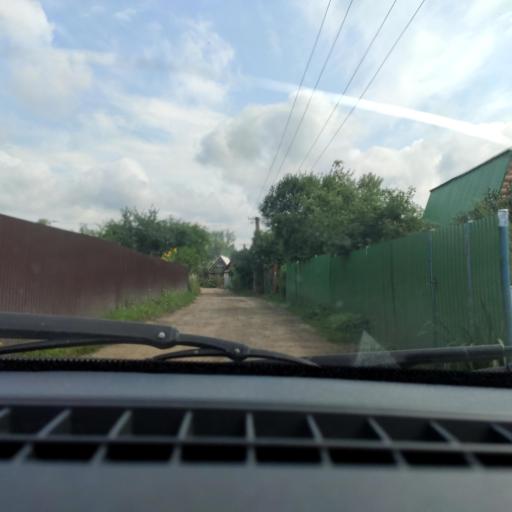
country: RU
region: Bashkortostan
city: Iglino
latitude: 54.7875
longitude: 56.2060
